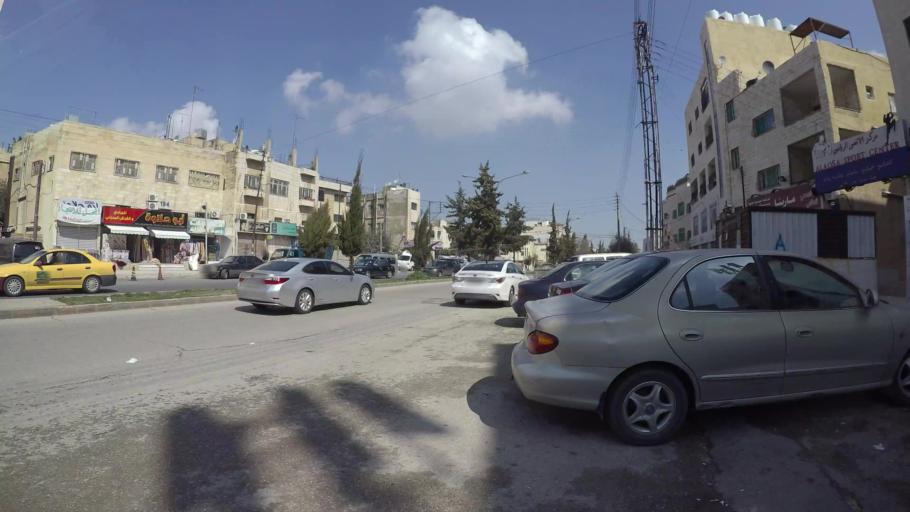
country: JO
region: Amman
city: Al Bunayyat ash Shamaliyah
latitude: 31.9266
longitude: 35.9054
